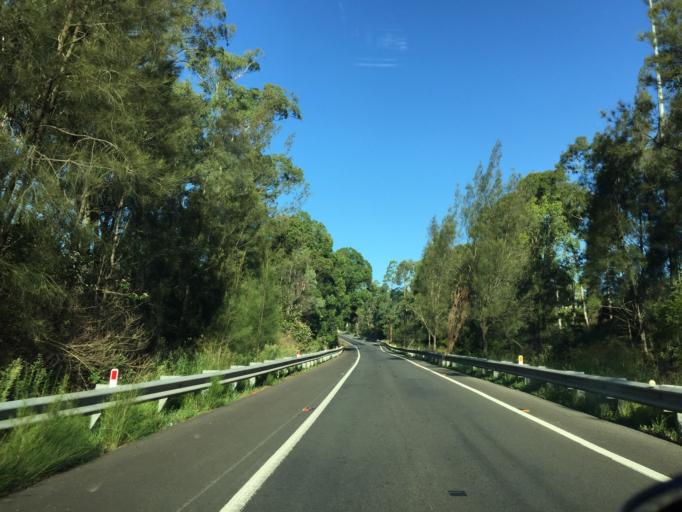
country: AU
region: New South Wales
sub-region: Blacktown
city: Blacktown
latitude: -33.8023
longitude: 150.8928
